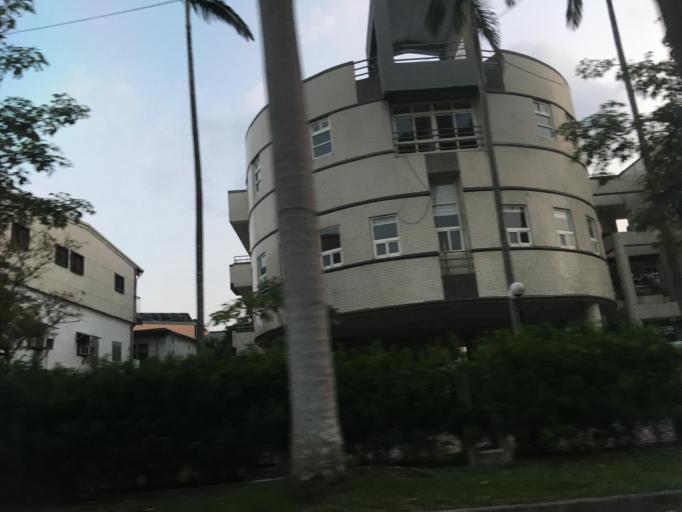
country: TW
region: Taiwan
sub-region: Yilan
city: Yilan
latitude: 24.6929
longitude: 121.7728
